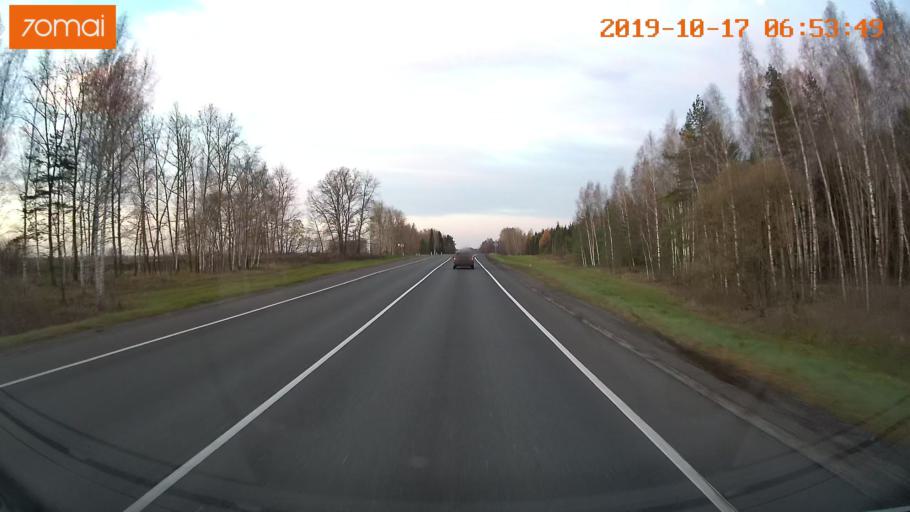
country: RU
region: Vladimir
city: Suzdal'
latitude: 56.4705
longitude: 40.4804
